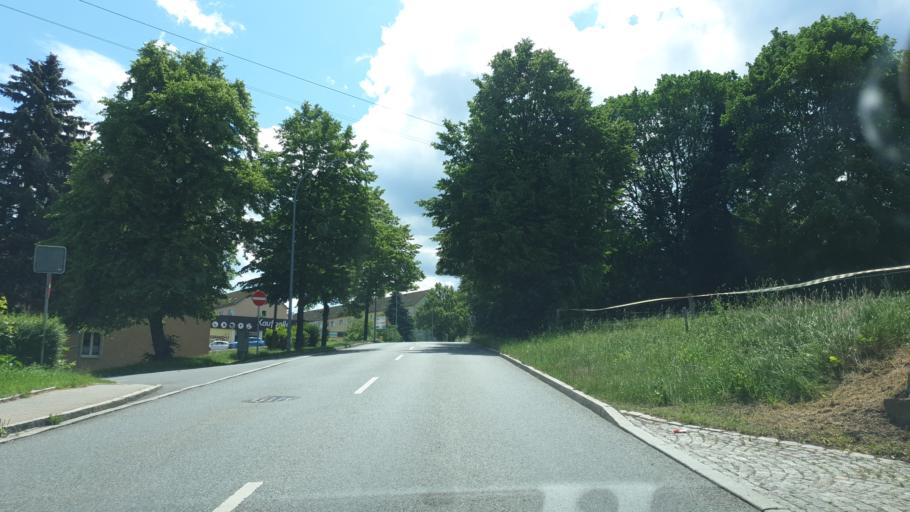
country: DE
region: Saxony
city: Schwarzenberg
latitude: 50.5421
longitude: 12.7778
